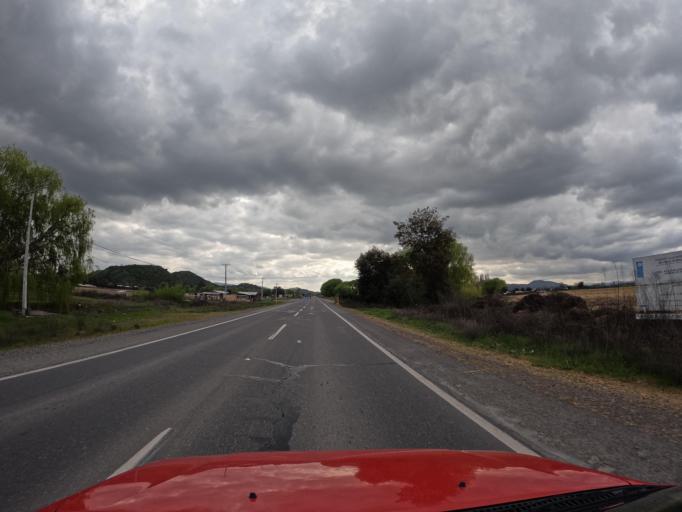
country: CL
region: Maule
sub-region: Provincia de Linares
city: San Javier
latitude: -35.6300
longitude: -71.7250
